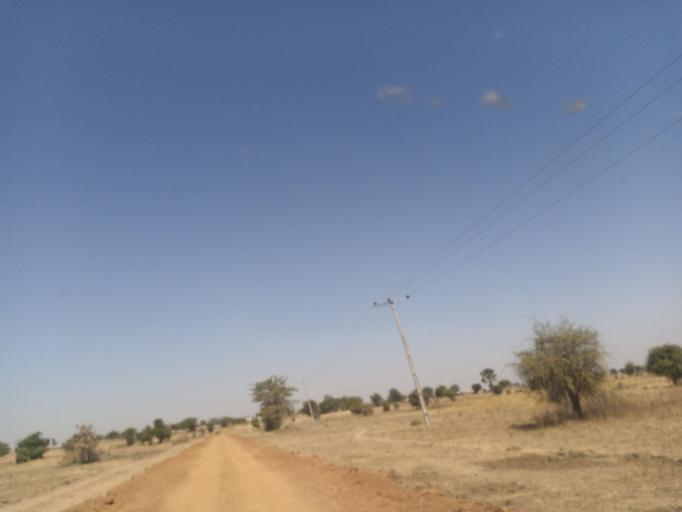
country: NG
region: Adamawa
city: Yola
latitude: 9.3059
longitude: 12.8897
